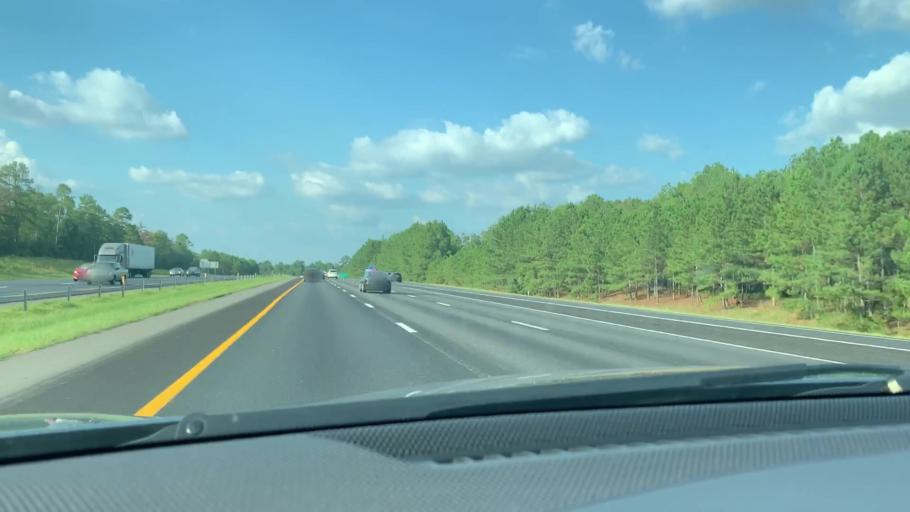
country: US
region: South Carolina
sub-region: Richland County
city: Forest Acres
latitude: 33.9822
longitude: -80.9537
